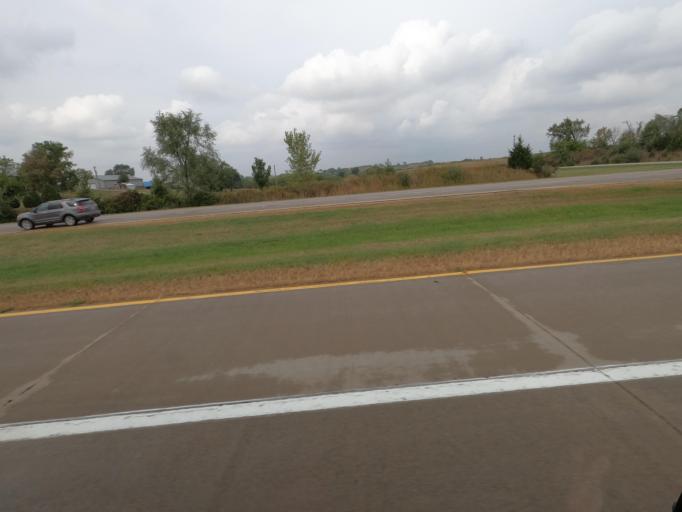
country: US
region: Iowa
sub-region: Wapello County
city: Ottumwa
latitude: 41.0962
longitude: -92.4870
